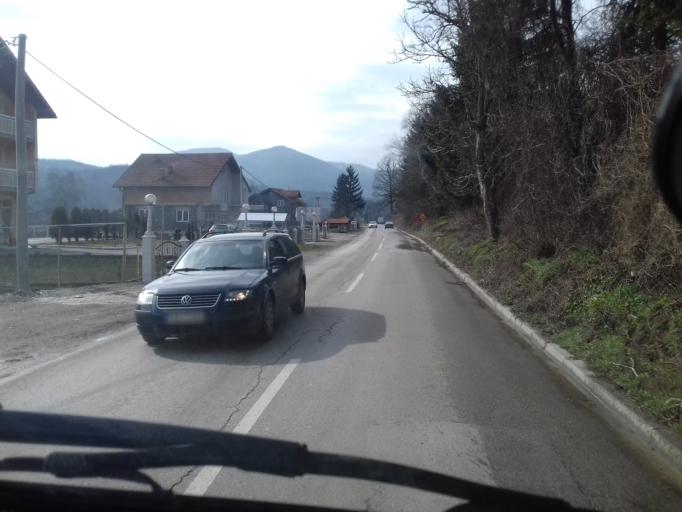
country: BA
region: Federation of Bosnia and Herzegovina
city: Visoko
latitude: 43.9947
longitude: 18.2052
